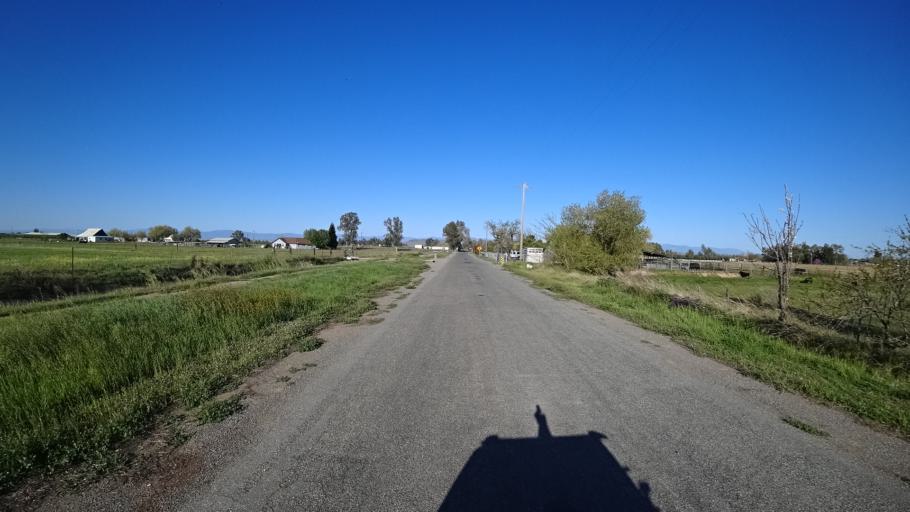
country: US
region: California
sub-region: Glenn County
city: Orland
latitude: 39.7550
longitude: -122.2361
